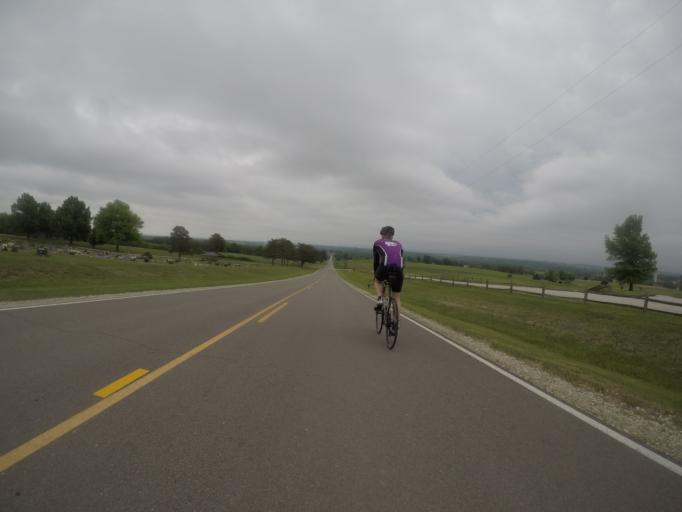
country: US
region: Kansas
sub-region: Pottawatomie County
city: Westmoreland
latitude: 39.5078
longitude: -96.1764
